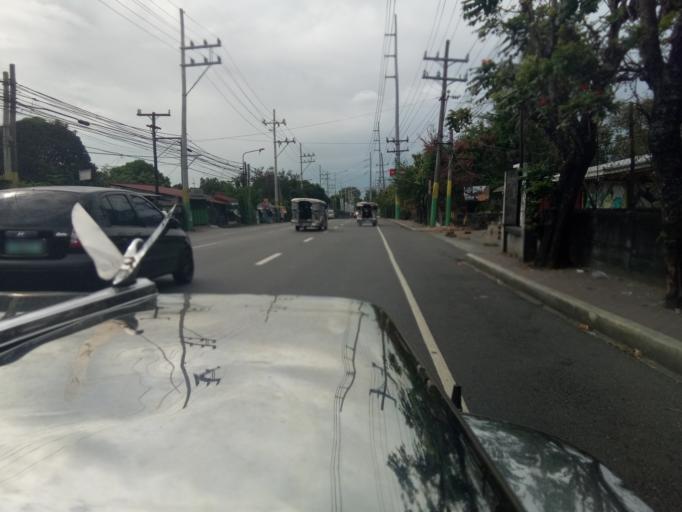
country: PH
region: Calabarzon
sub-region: Province of Cavite
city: Dasmarinas
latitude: 14.3051
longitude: 120.9535
